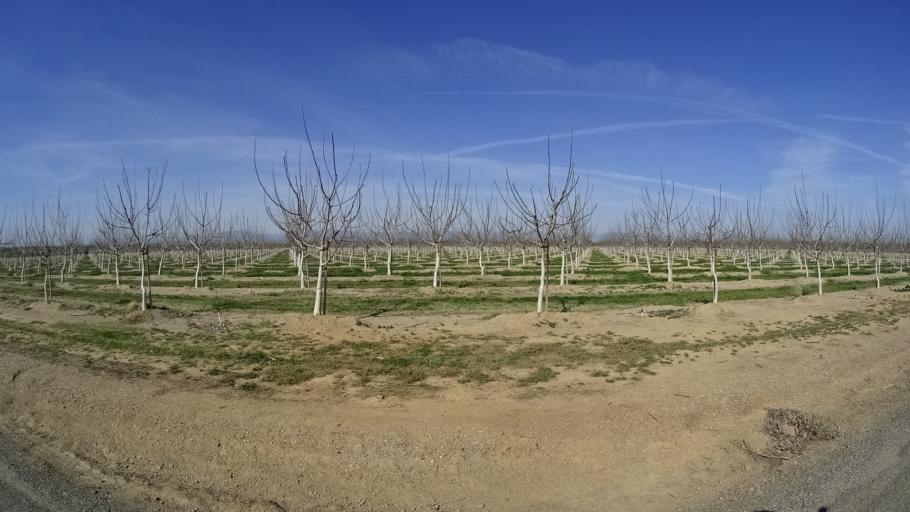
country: US
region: California
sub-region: Glenn County
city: Willows
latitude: 39.6138
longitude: -122.2129
